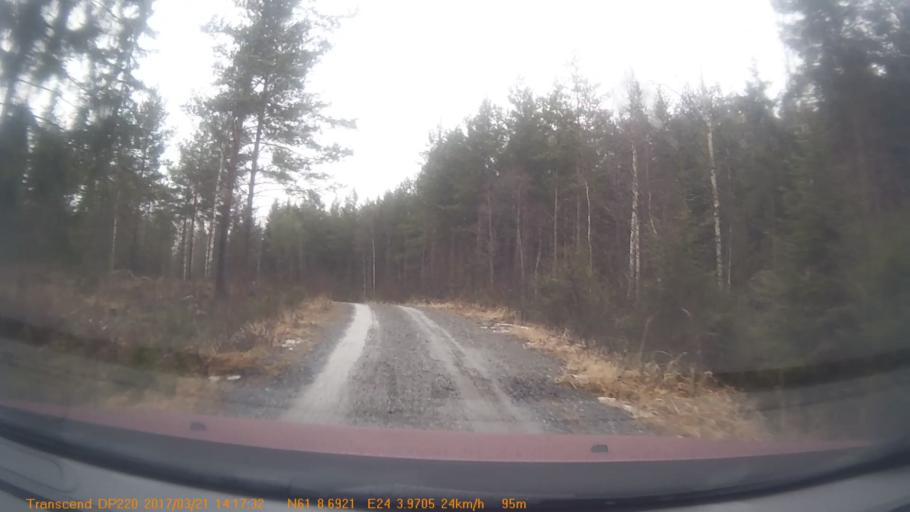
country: FI
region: Haeme
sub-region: Haemeenlinna
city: Kalvola
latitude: 61.1448
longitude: 24.0662
